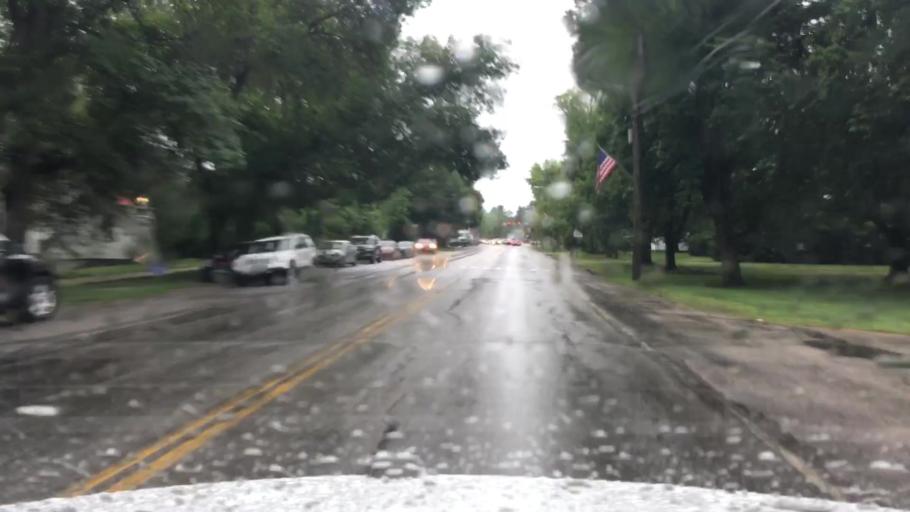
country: US
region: Maine
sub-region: Oxford County
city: Fryeburg
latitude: 44.0186
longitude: -70.9783
